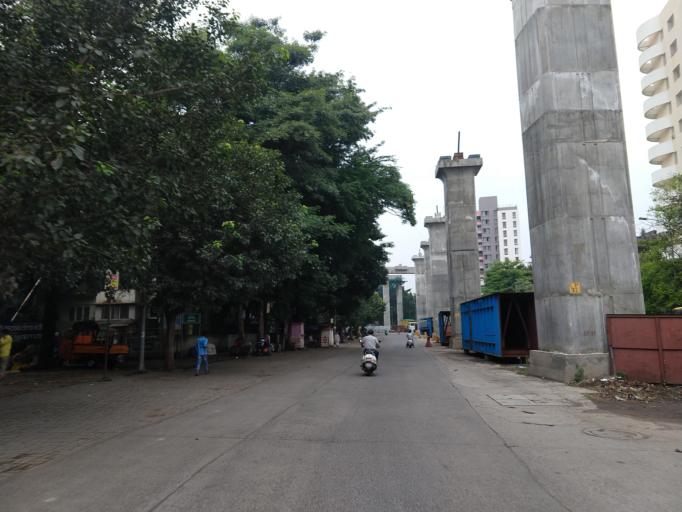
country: IN
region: Maharashtra
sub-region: Pune Division
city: Pune
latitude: 18.5083
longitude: 73.8103
